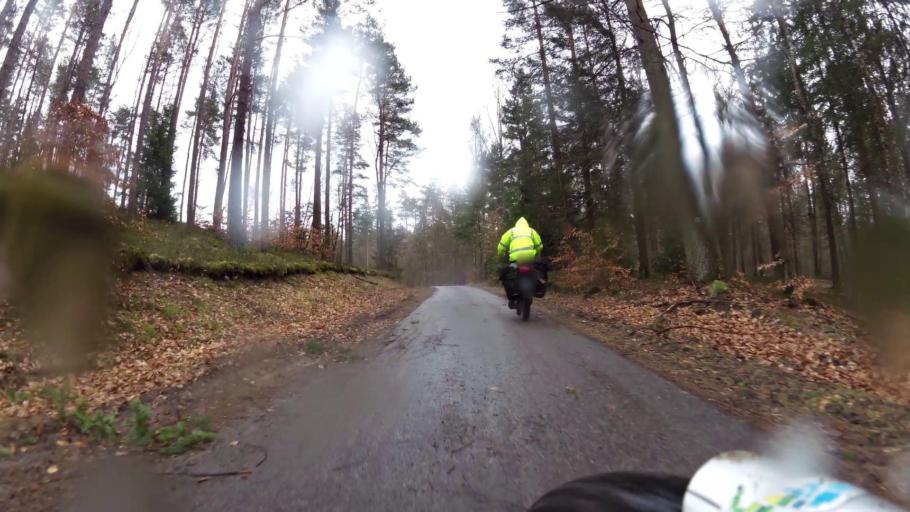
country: PL
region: Pomeranian Voivodeship
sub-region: Powiat bytowski
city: Miastko
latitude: 54.0645
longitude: 17.0767
